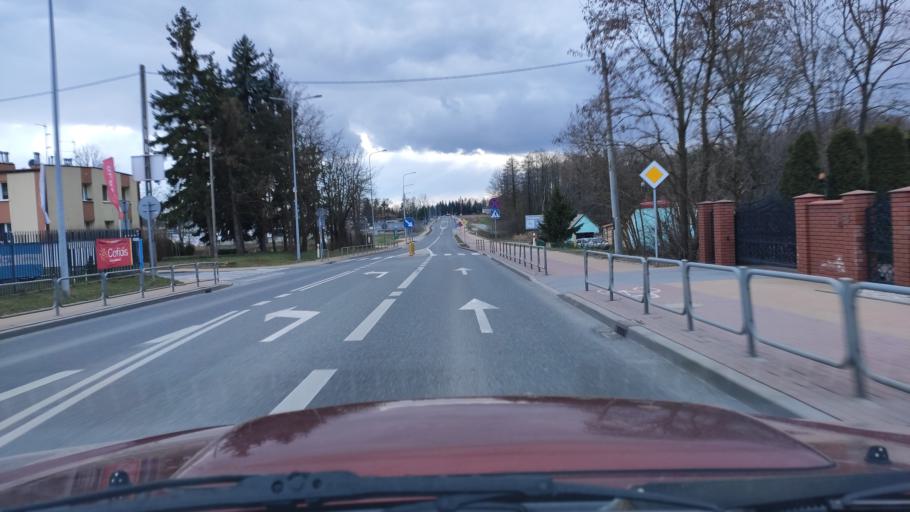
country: PL
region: Masovian Voivodeship
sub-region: Powiat zwolenski
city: Zwolen
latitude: 51.3763
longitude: 21.5939
